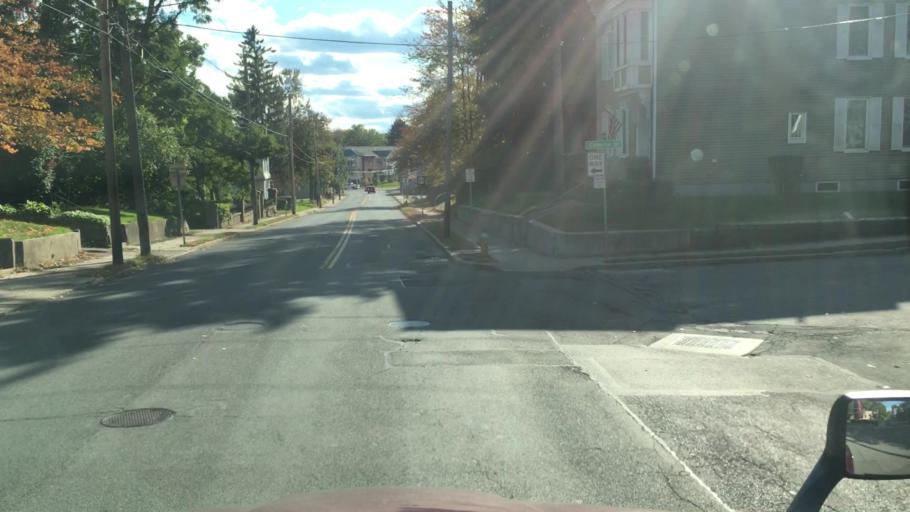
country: US
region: New York
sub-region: Schenectady County
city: Scotia
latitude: 42.8275
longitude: -73.9608
